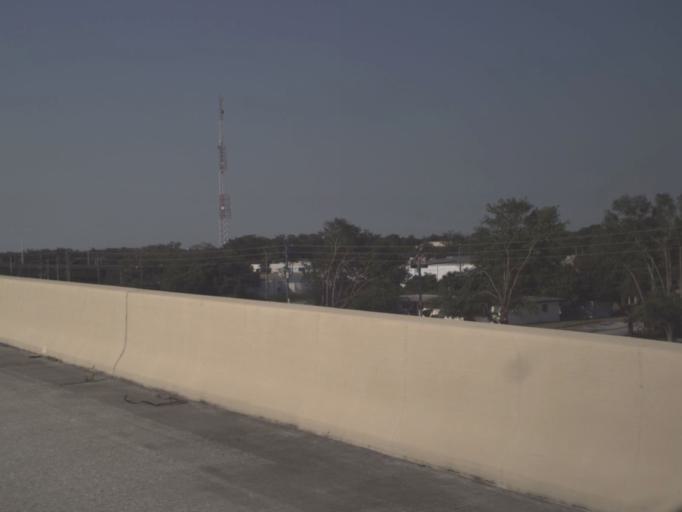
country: US
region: Florida
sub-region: Orange County
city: Fairview Shores
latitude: 28.6001
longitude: -81.4173
